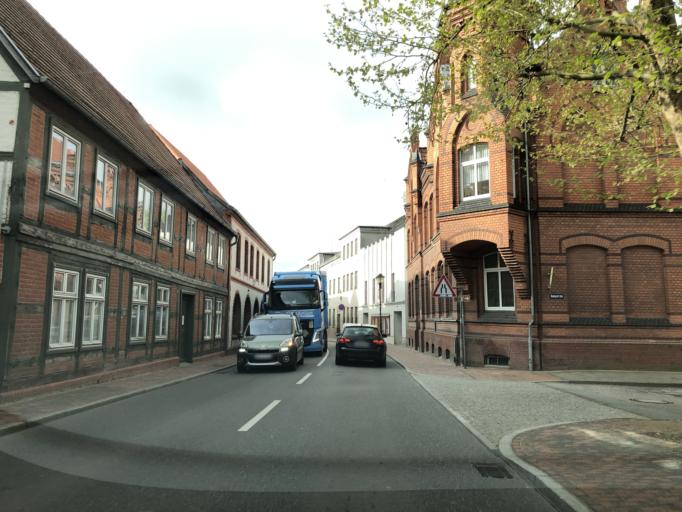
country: DE
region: Mecklenburg-Vorpommern
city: Goldberg
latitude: 53.5881
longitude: 12.0878
